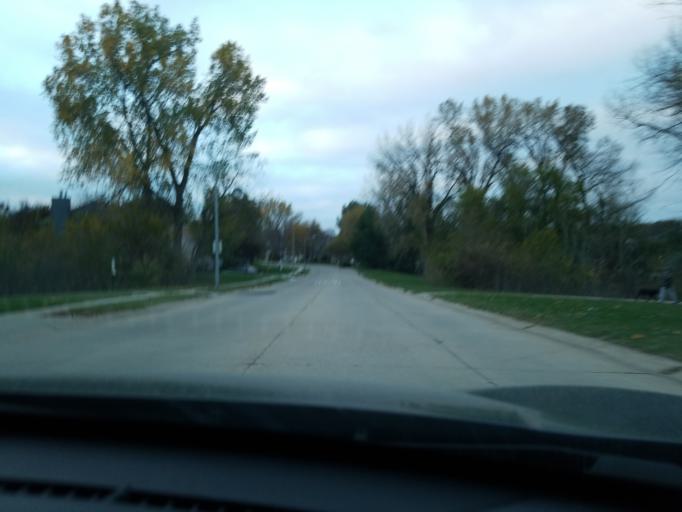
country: US
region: Nebraska
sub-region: Sarpy County
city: La Vista
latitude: 41.1693
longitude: -96.0286
